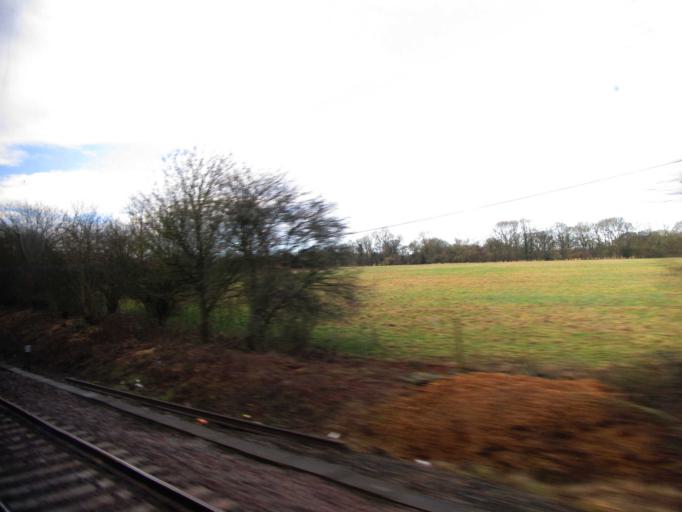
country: GB
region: England
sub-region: Hampshire
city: Old Basing
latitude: 51.3034
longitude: -1.0555
